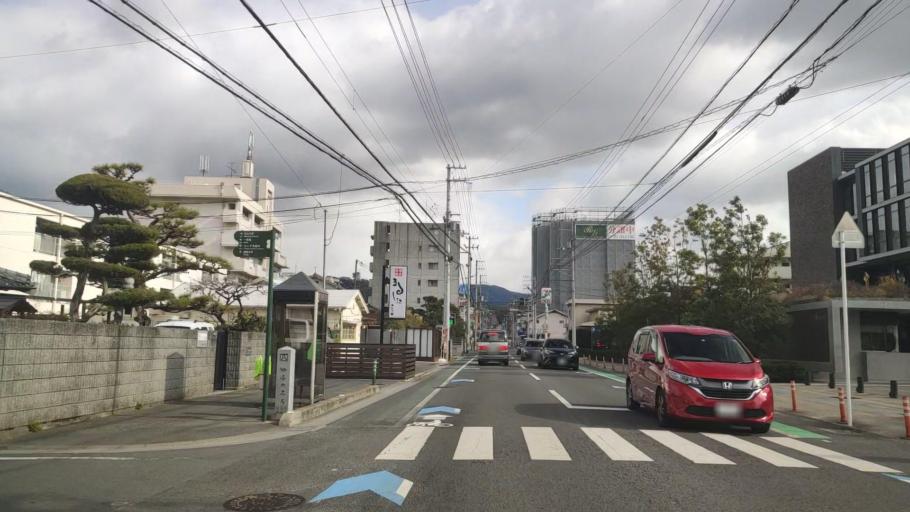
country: JP
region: Ehime
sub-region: Shikoku-chuo Shi
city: Matsuyama
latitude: 33.8524
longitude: 132.7687
